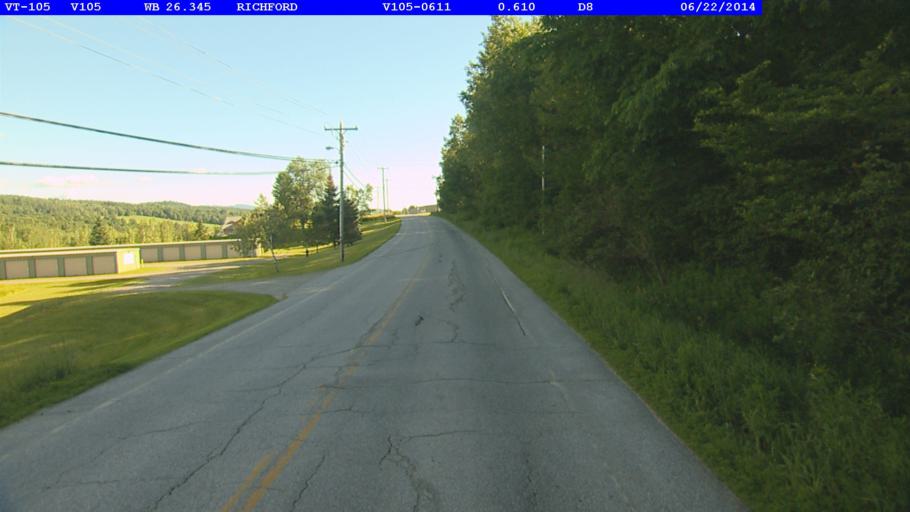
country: US
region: Vermont
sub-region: Franklin County
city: Richford
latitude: 44.9793
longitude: -72.6869
